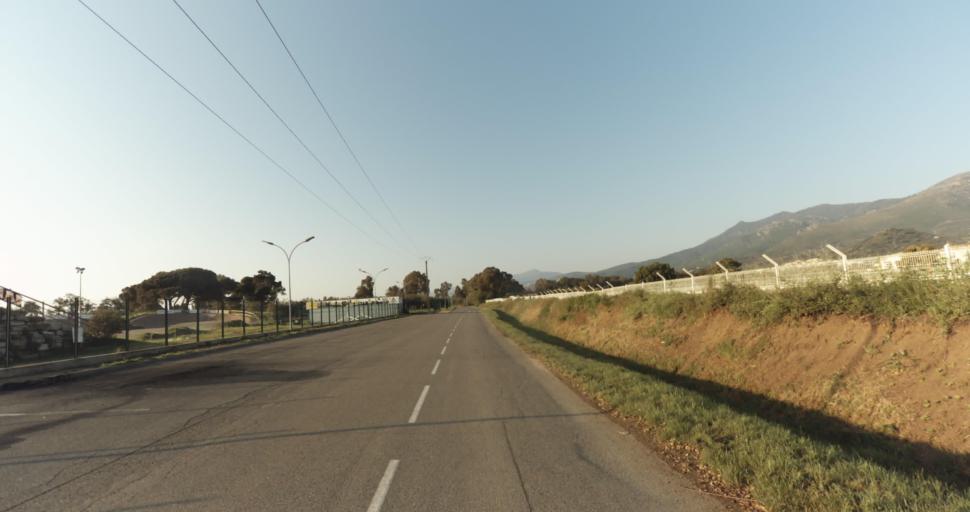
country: FR
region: Corsica
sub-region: Departement de la Haute-Corse
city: Biguglia
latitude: 42.6186
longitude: 9.4433
